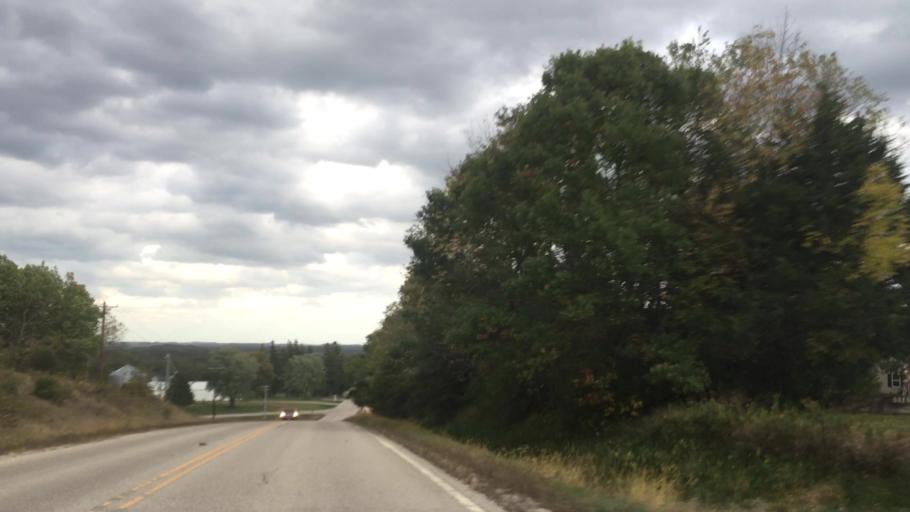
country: US
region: Minnesota
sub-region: Fillmore County
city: Preston
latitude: 43.7344
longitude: -92.0088
